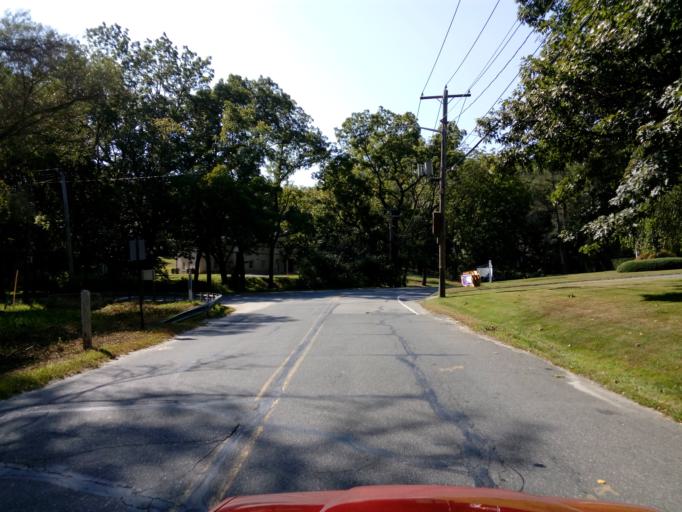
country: US
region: New York
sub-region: Nassau County
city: Upper Brookville
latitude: 40.8280
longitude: -73.5701
